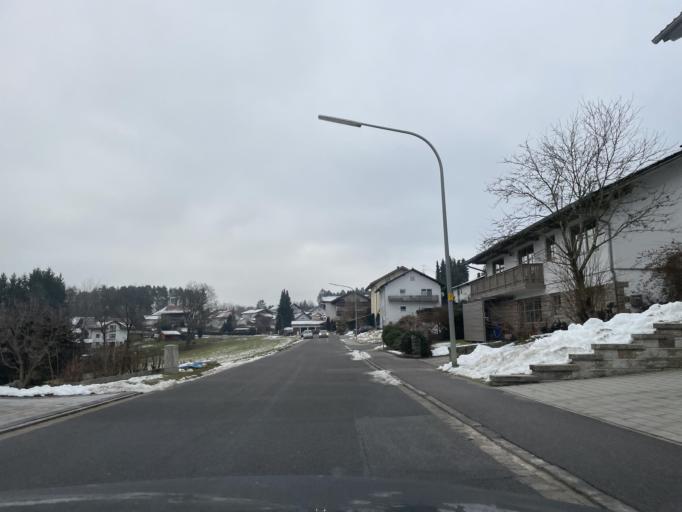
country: DE
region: Bavaria
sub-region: Lower Bavaria
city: Viechtach
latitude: 49.0679
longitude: 12.8997
